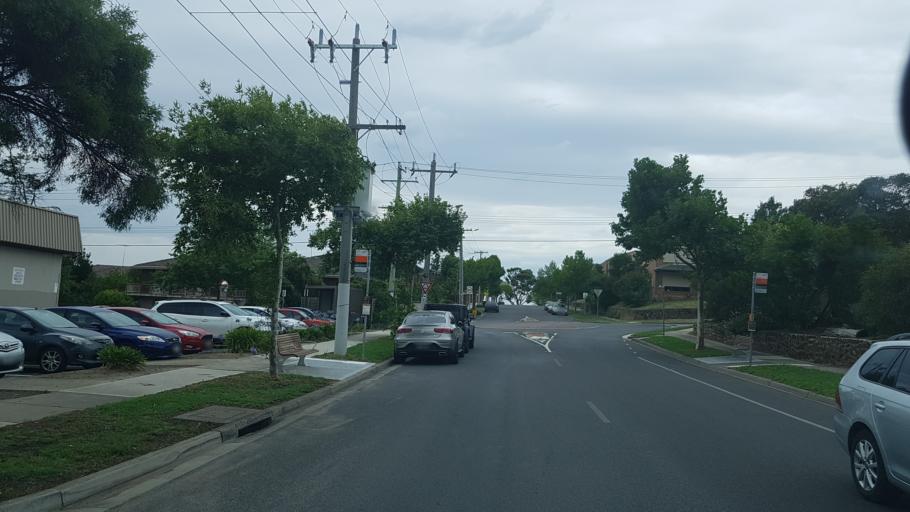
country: AU
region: Victoria
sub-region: Manningham
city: Bulleen
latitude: -37.7657
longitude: 145.0929
